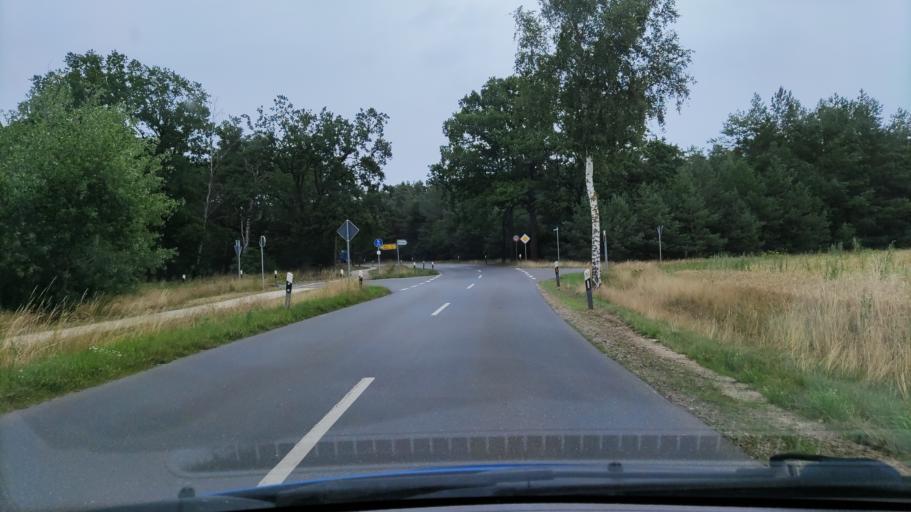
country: DE
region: Lower Saxony
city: Rosche
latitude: 52.9988
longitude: 10.7681
